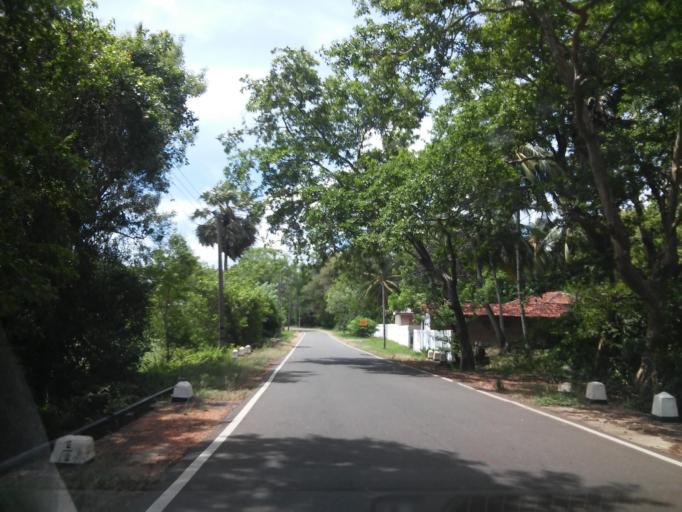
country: LK
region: North Central
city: Anuradhapura
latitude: 8.3687
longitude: 80.4005
